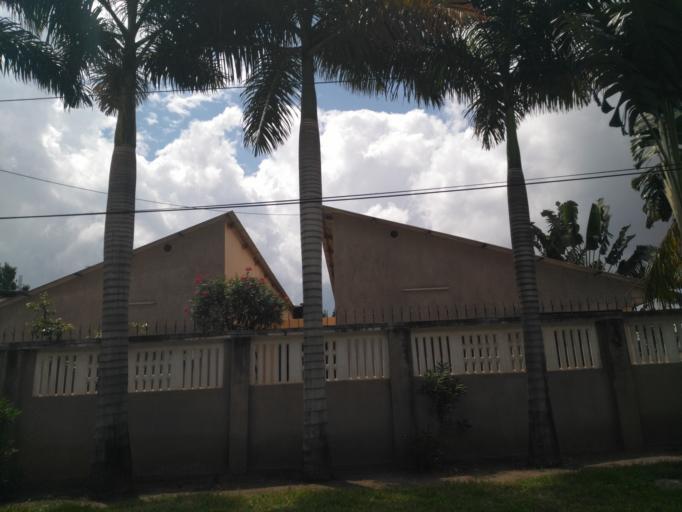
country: TZ
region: Dar es Salaam
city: Magomeni
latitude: -6.7617
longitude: 39.2492
